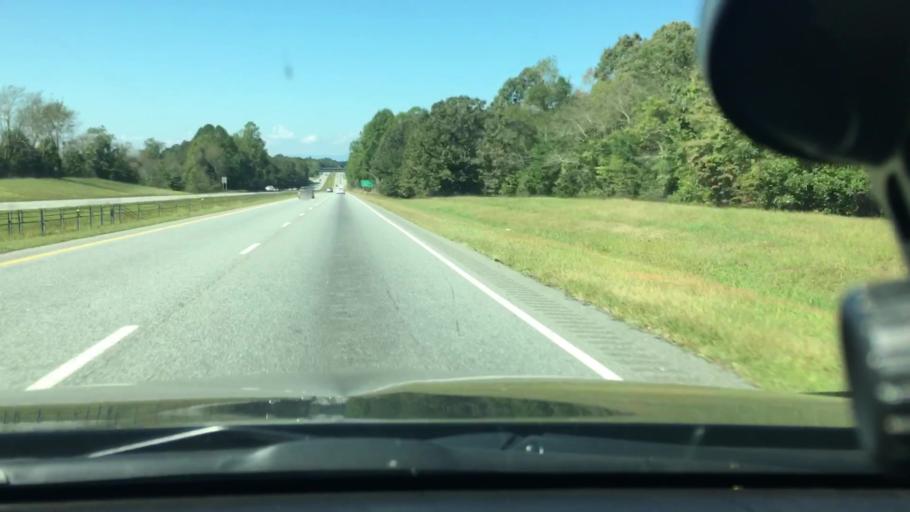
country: US
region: North Carolina
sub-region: Cleveland County
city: Boiling Springs
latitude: 35.3017
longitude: -81.7603
